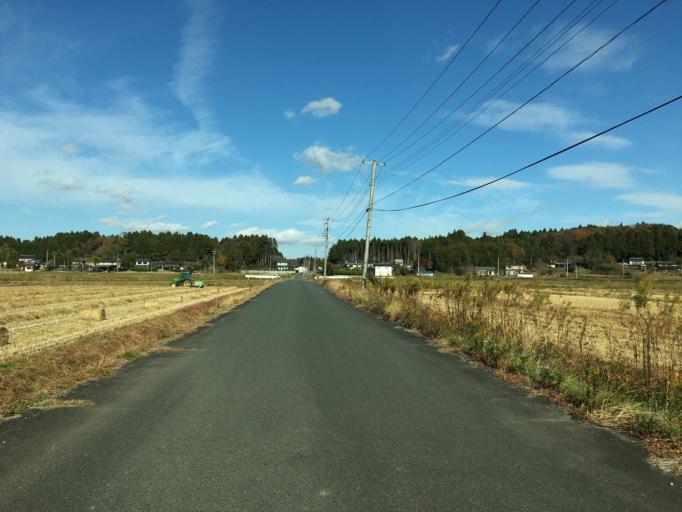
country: JP
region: Miyagi
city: Marumori
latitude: 37.8910
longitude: 140.9115
